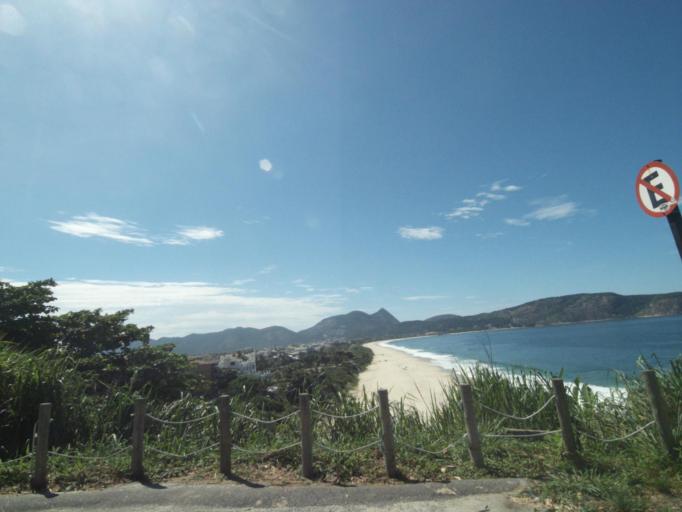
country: BR
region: Rio de Janeiro
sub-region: Niteroi
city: Niteroi
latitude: -22.9586
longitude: -43.0688
